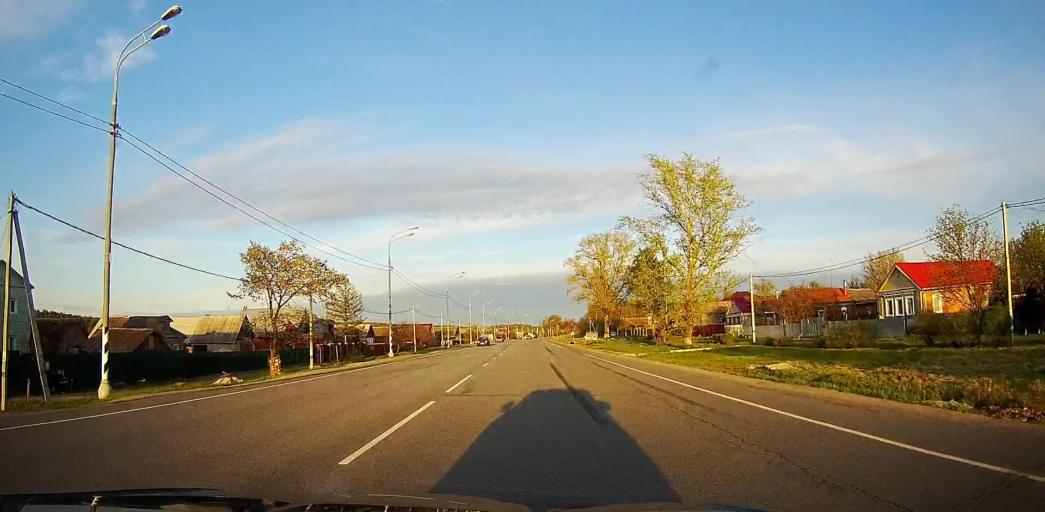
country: RU
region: Moskovskaya
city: Troitskoye
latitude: 55.2247
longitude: 38.5663
